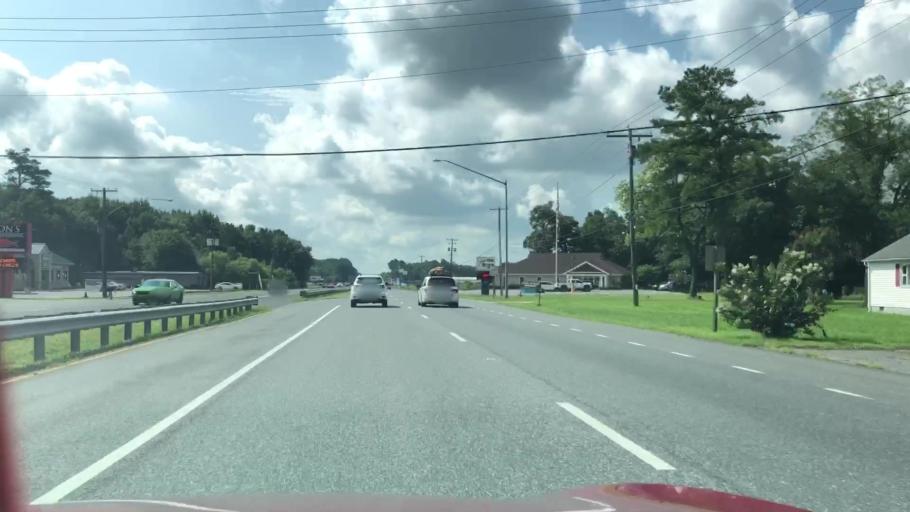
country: US
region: Maryland
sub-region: Worcester County
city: Pocomoke City
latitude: 38.0511
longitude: -75.5435
